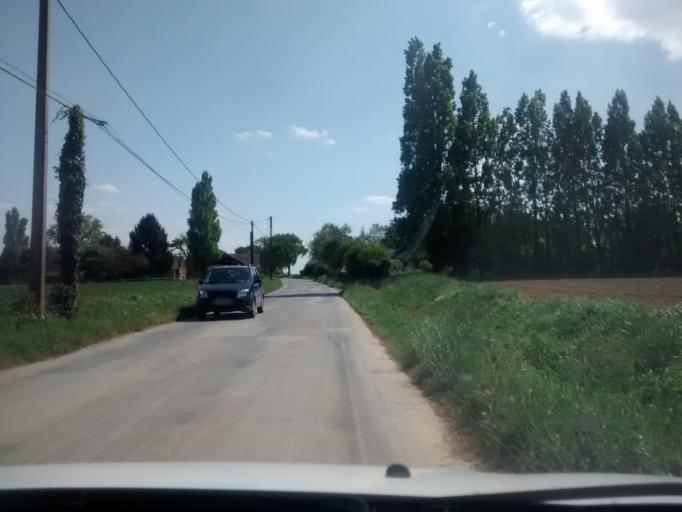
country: FR
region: Brittany
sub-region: Departement d'Ille-et-Vilaine
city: Cesson-Sevigne
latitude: 48.1445
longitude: -1.6069
